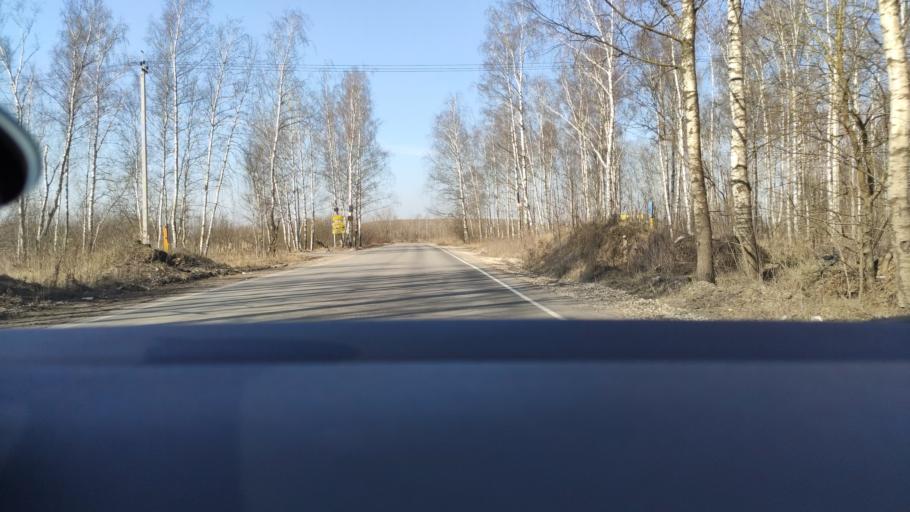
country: RU
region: Moskovskaya
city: Elektrostal'
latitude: 55.7639
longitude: 38.3896
